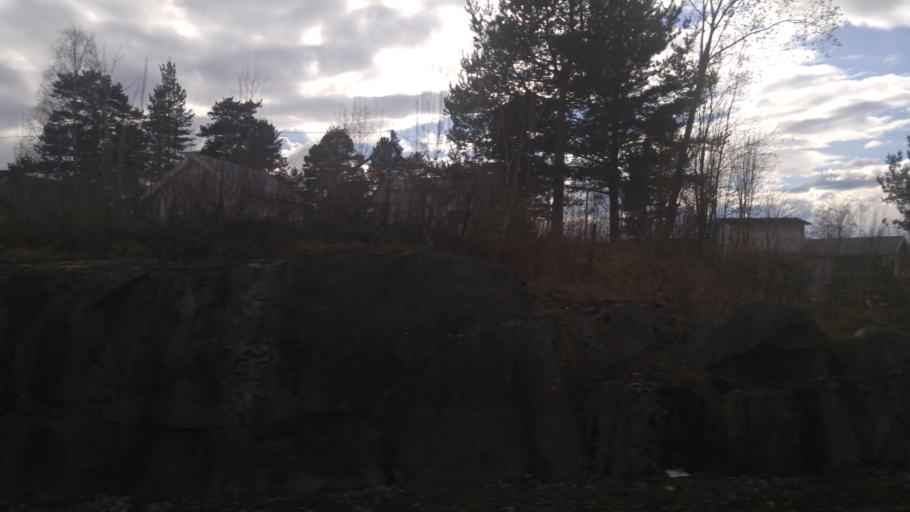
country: NO
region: Hedmark
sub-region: Stange
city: Stange
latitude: 60.6151
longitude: 11.2708
